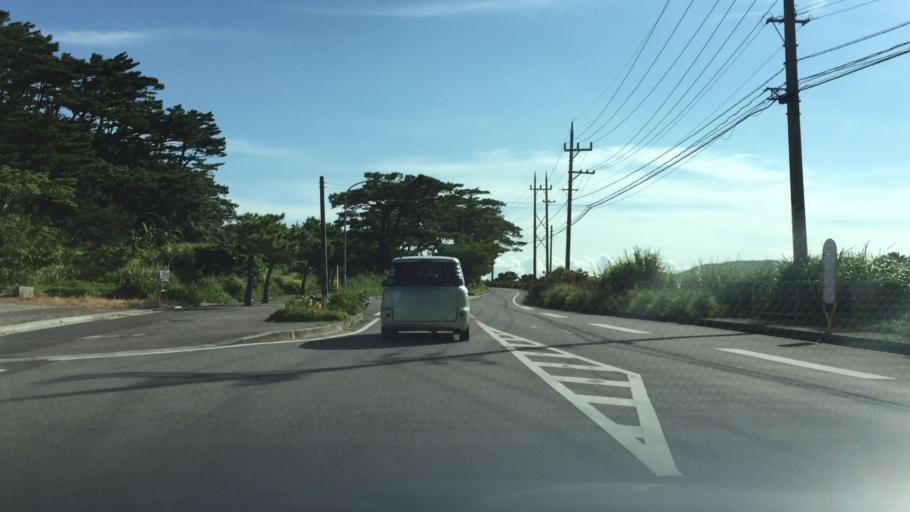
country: JP
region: Okinawa
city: Ishigaki
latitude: 24.4466
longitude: 124.1272
